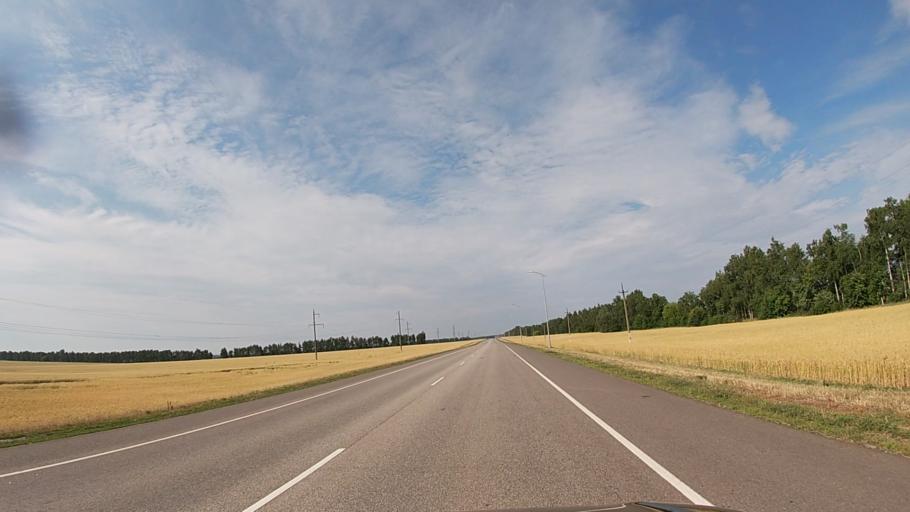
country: RU
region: Belgorod
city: Proletarskiy
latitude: 50.8261
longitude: 35.7606
